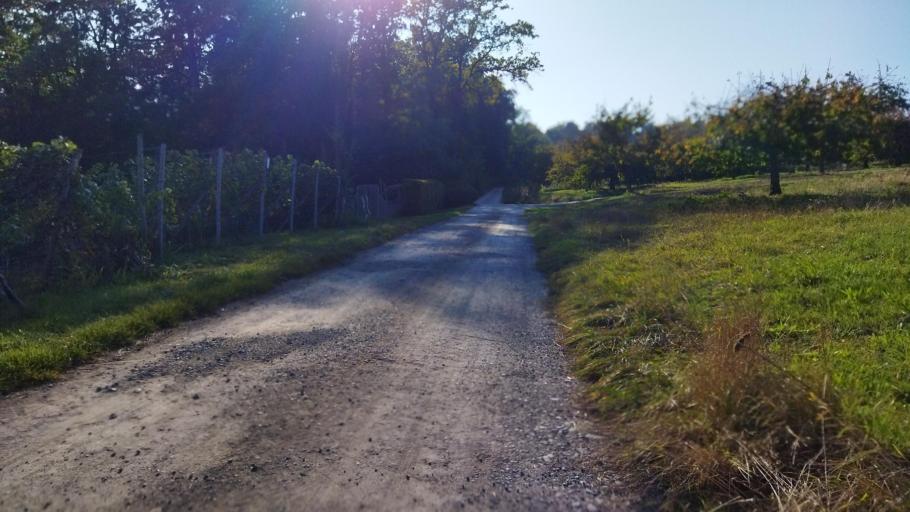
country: DE
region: Baden-Wuerttemberg
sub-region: Regierungsbezirk Stuttgart
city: Freudental
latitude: 49.0165
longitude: 9.0739
